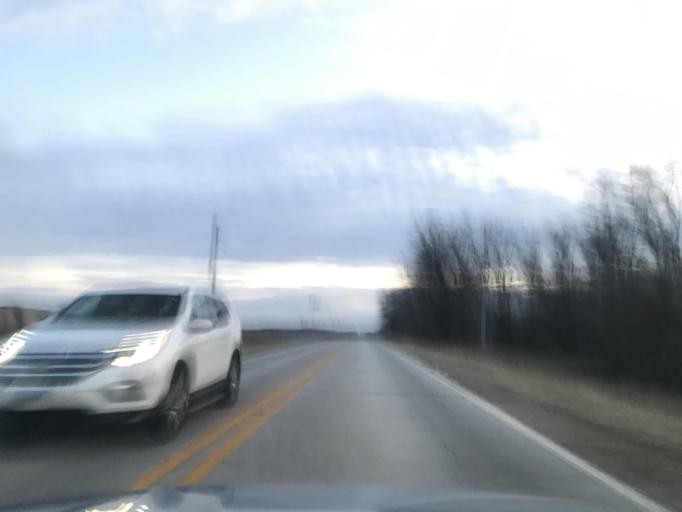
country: US
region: Iowa
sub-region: Des Moines County
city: Burlington
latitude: 40.6943
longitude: -91.0702
